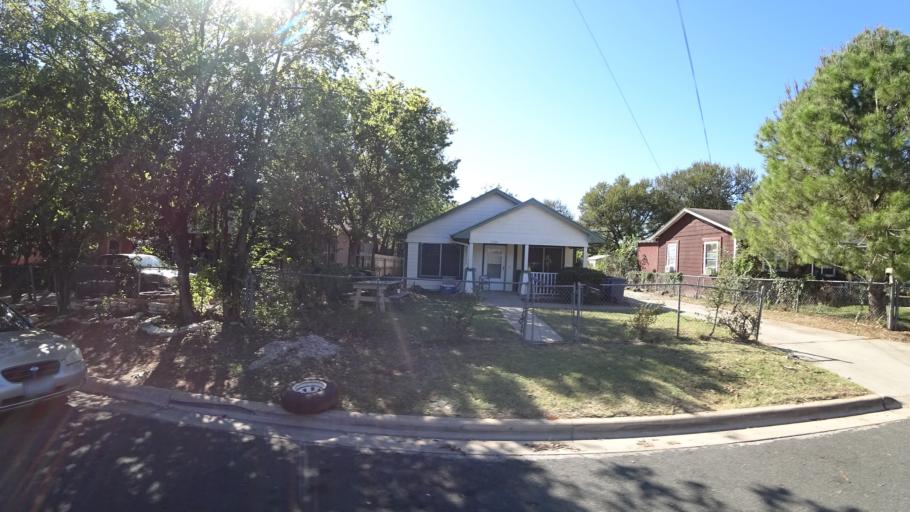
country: US
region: Texas
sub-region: Travis County
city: Austin
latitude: 30.2795
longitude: -97.6920
